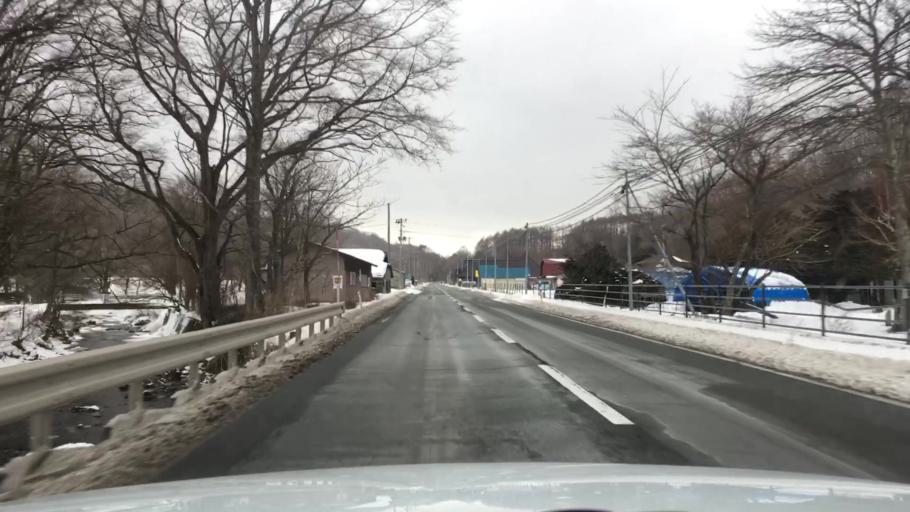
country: JP
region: Iwate
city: Morioka-shi
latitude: 39.6415
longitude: 141.4146
